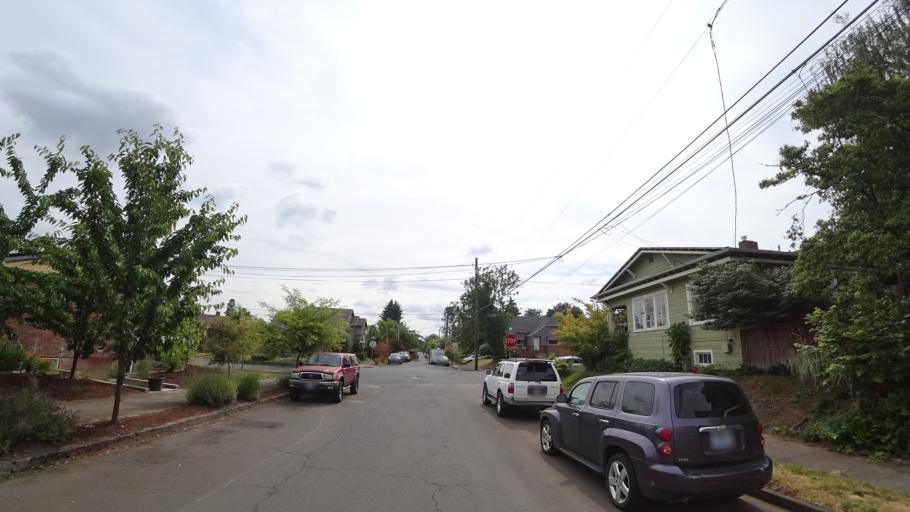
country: US
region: Oregon
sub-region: Multnomah County
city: Portland
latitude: 45.5751
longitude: -122.6753
